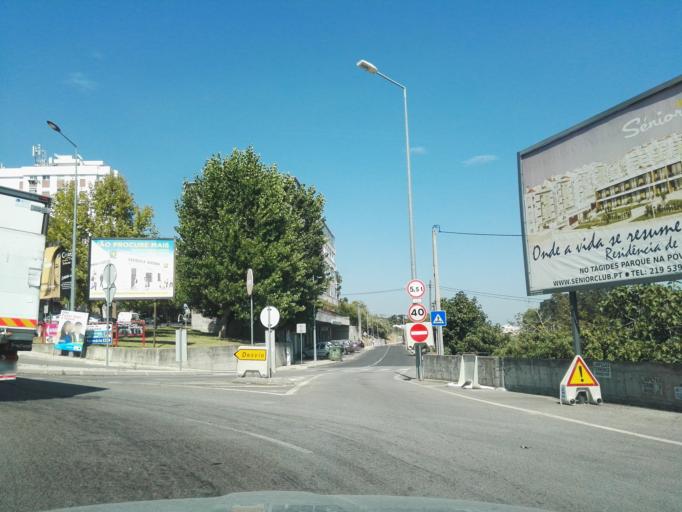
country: PT
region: Lisbon
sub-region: Vila Franca de Xira
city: Povoa de Santa Iria
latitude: 38.8550
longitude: -9.0715
